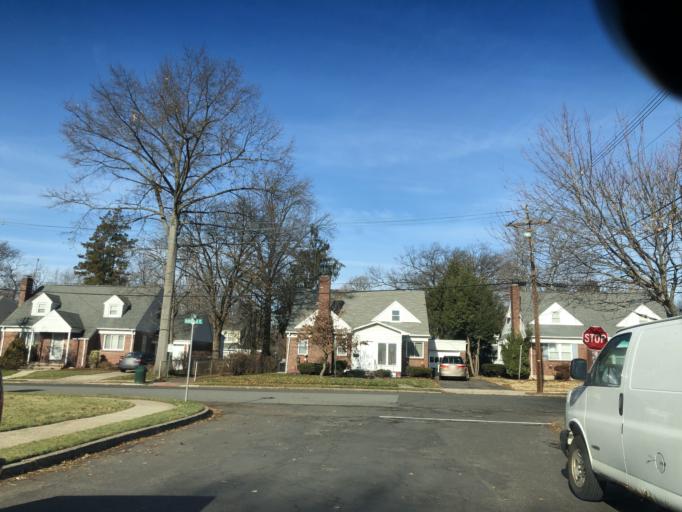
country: US
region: New Jersey
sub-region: Bergen County
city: Fair Lawn
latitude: 40.9253
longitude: -74.1233
